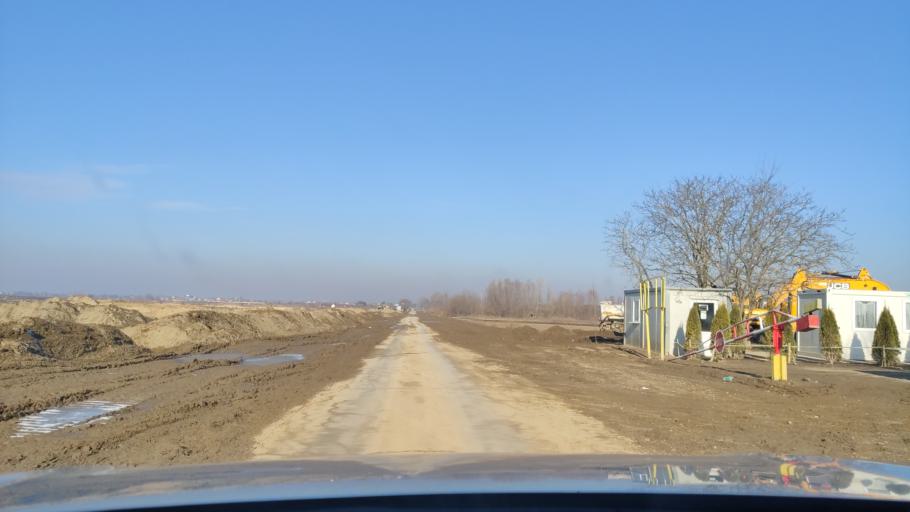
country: RS
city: Ostruznica
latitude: 44.7324
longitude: 20.2804
